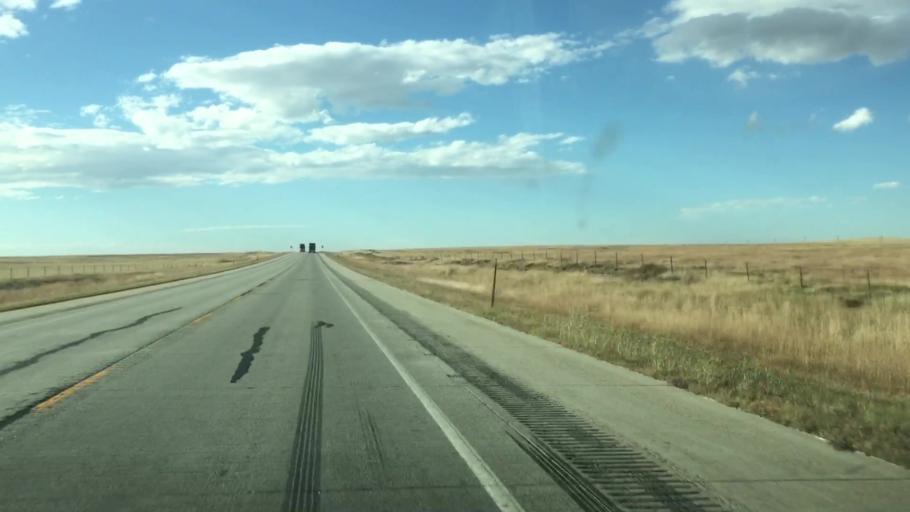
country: US
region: Colorado
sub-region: Lincoln County
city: Hugo
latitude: 39.1839
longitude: -103.5511
